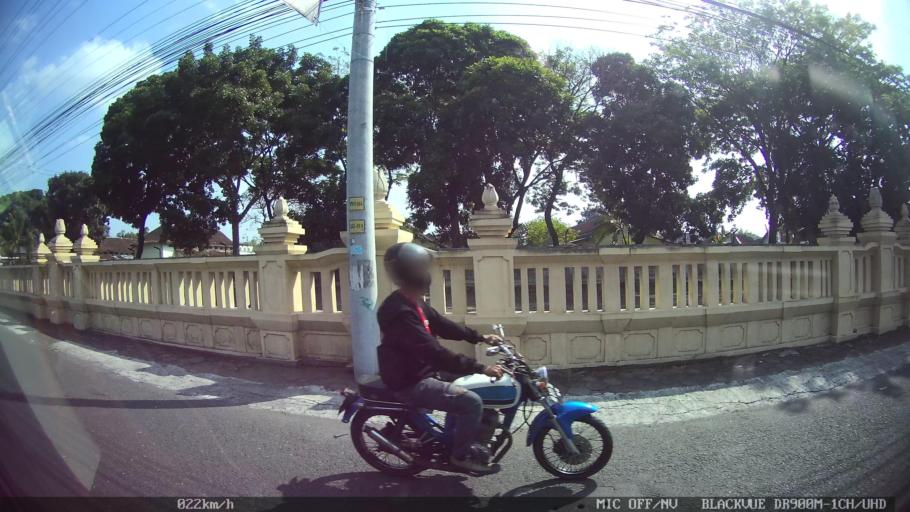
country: ID
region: Daerah Istimewa Yogyakarta
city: Melati
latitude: -7.7552
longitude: 110.3891
